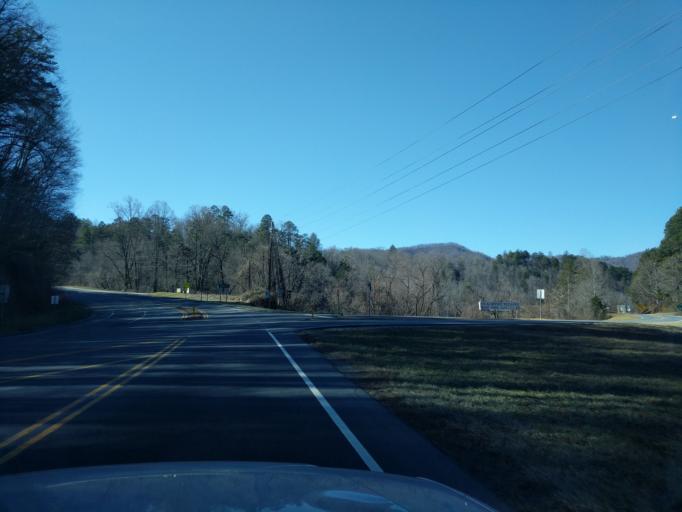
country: US
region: North Carolina
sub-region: Swain County
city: Bryson City
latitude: 35.3646
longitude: -83.5513
